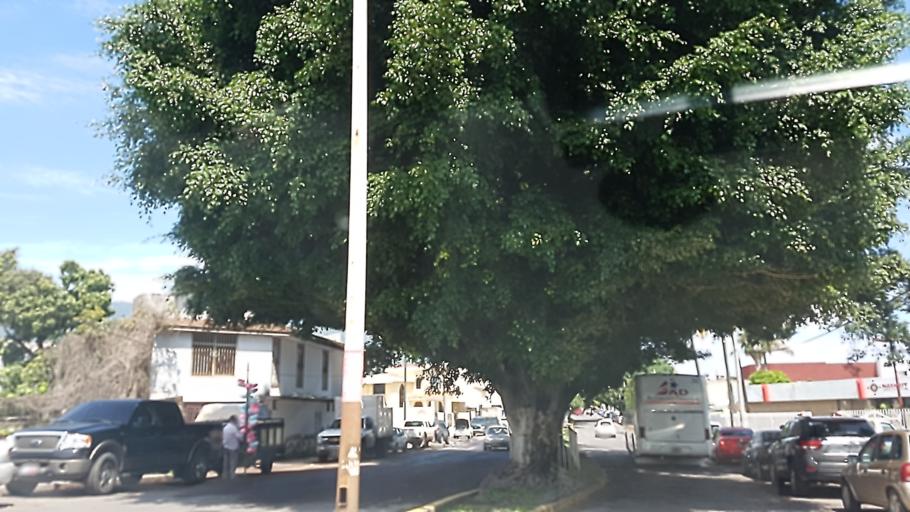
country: MX
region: Nayarit
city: Tepic
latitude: 21.4840
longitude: -104.8805
